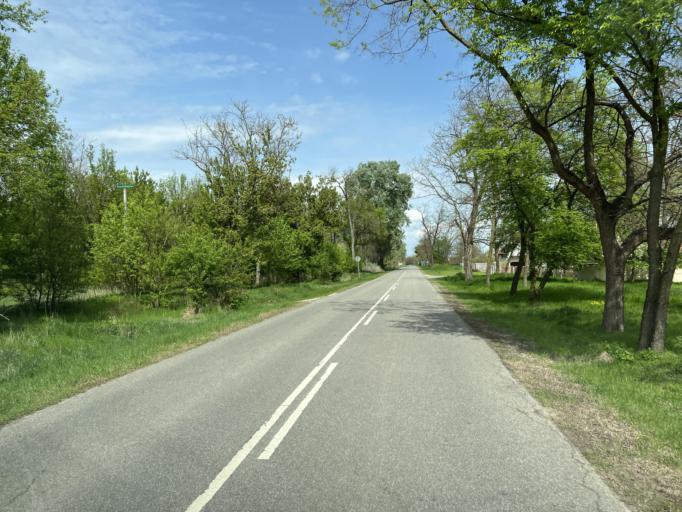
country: HU
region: Pest
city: Albertirsa
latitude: 47.1588
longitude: 19.6116
